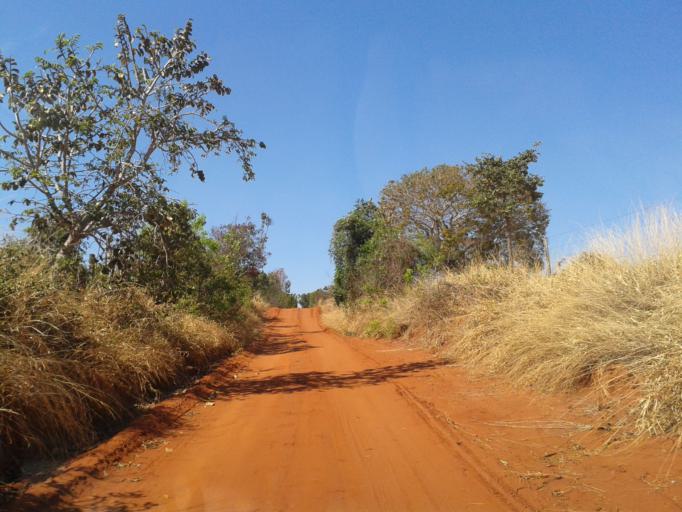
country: BR
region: Minas Gerais
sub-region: Ituiutaba
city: Ituiutaba
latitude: -19.0172
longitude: -49.2168
